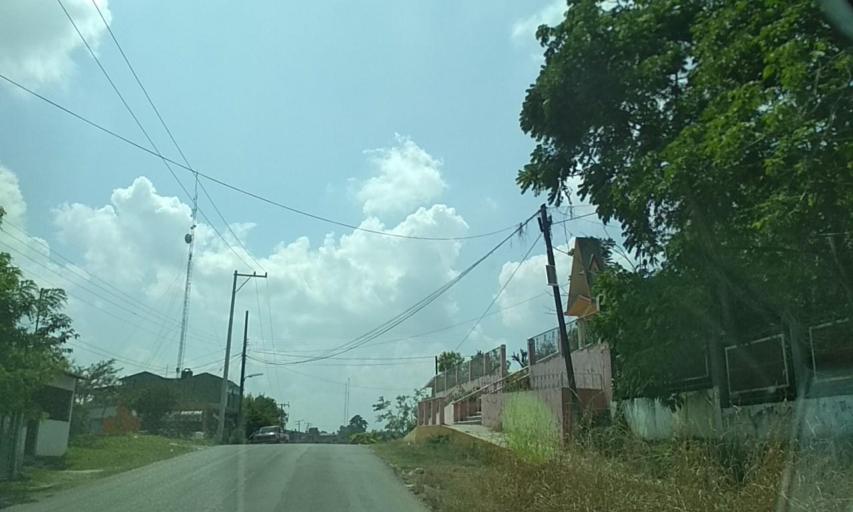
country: MX
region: Puebla
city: San Jose Acateno
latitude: 20.1741
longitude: -97.1122
